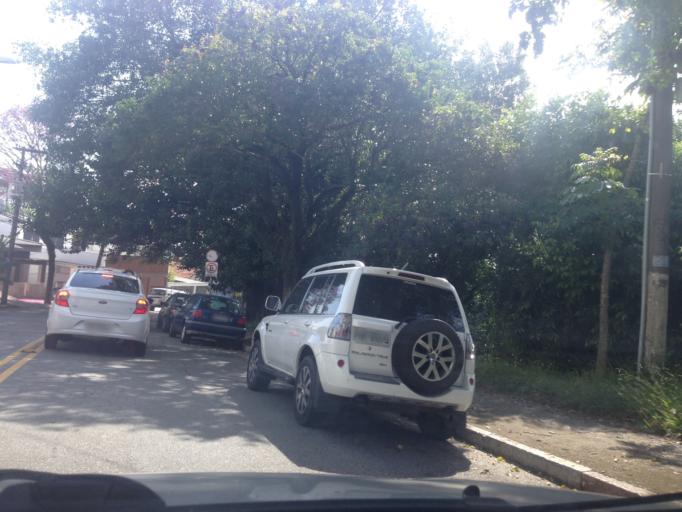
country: BR
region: Sao Paulo
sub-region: Sao Paulo
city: Sao Paulo
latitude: -23.5320
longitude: -46.7096
